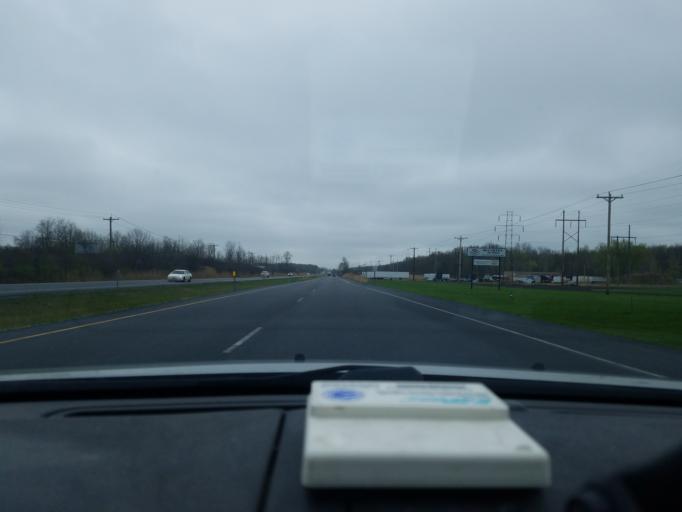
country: US
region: New York
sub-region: Onondaga County
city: North Syracuse
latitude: 43.1252
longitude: -76.0788
